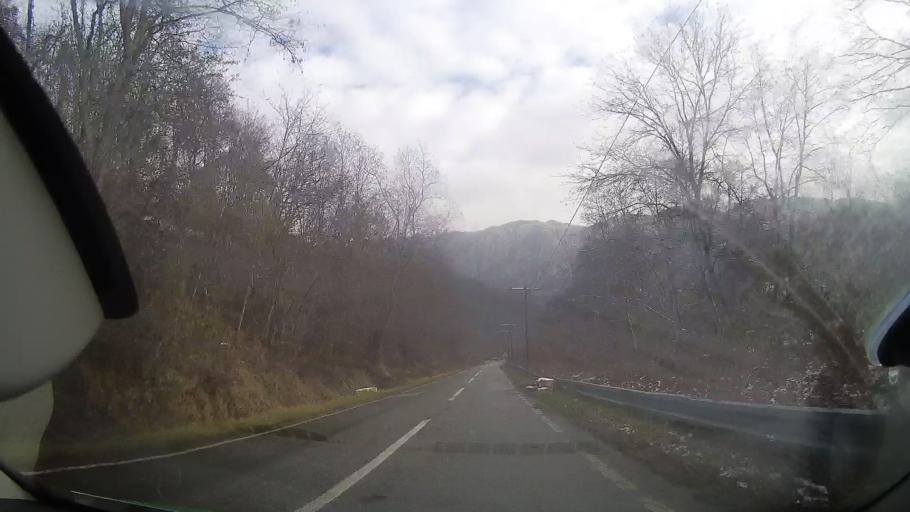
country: RO
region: Alba
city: Salciua de Sus
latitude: 46.4062
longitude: 23.4423
